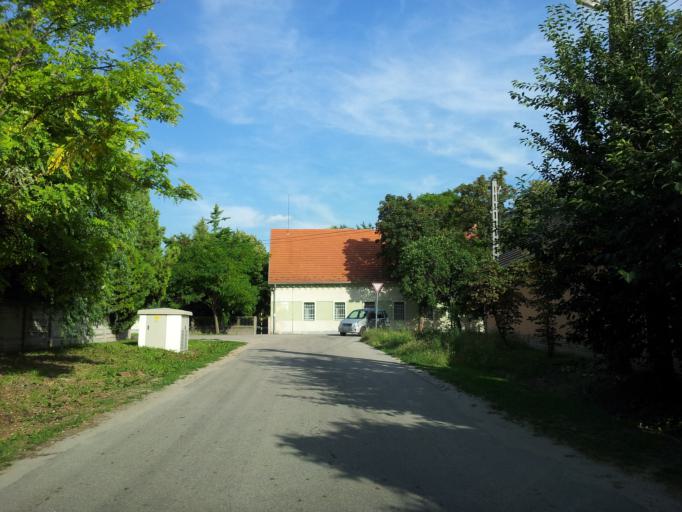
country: HU
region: Pest
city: Kiskunlachaza
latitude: 47.1918
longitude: 19.0042
